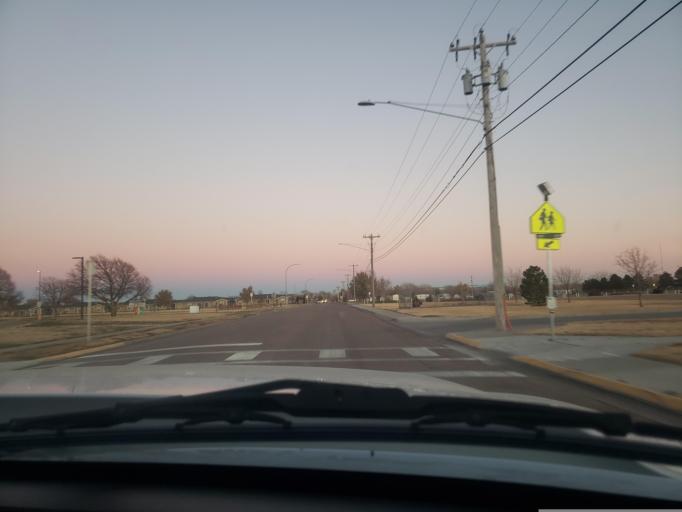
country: US
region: Kansas
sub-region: Finney County
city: Garden City
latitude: 37.9676
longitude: -100.8325
